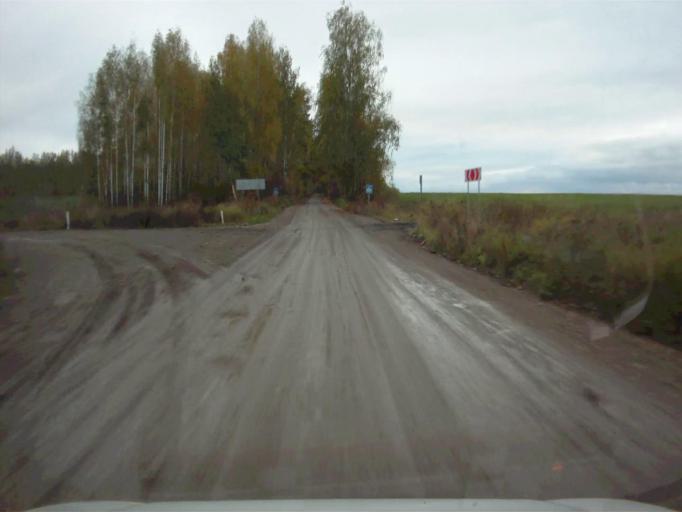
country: RU
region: Sverdlovsk
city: Mikhaylovsk
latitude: 56.1695
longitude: 59.2263
